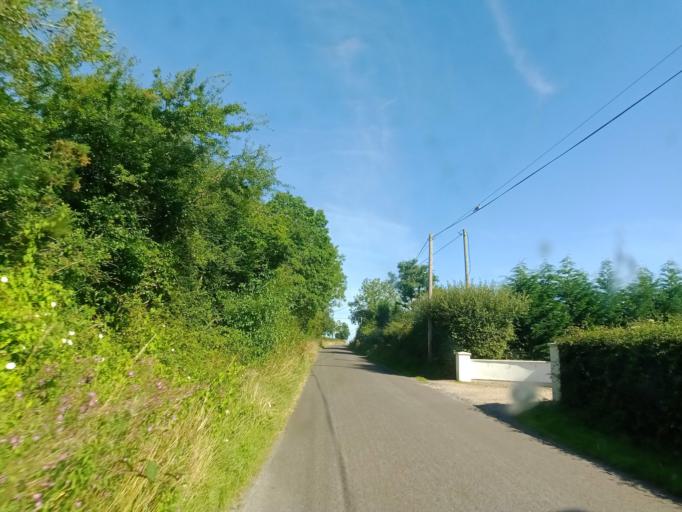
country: IE
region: Leinster
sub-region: Kilkenny
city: Ballyragget
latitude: 52.7637
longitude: -7.4082
